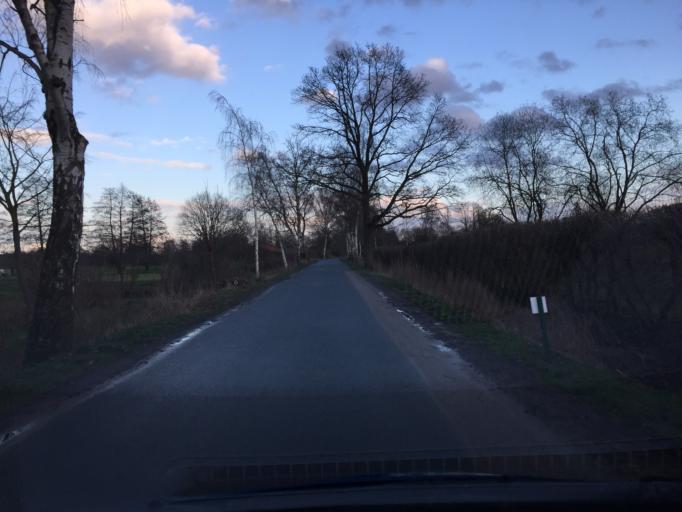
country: DE
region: Lower Saxony
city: Ludersburg
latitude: 53.3239
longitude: 10.5719
